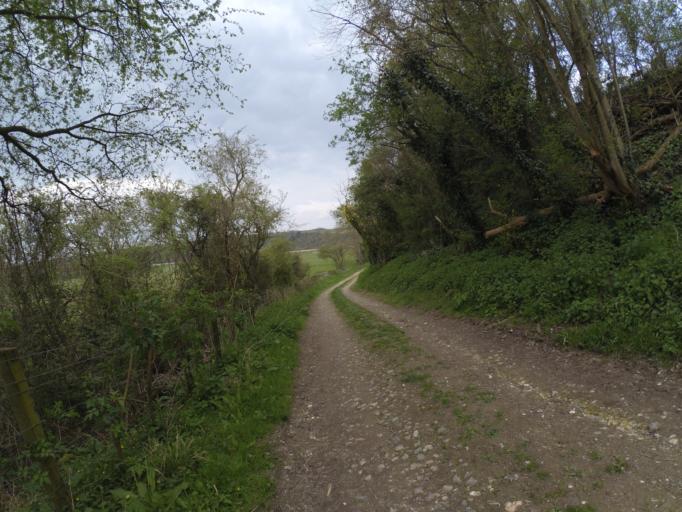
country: GB
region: England
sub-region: West Sussex
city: Arundel
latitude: 50.8789
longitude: -0.5307
